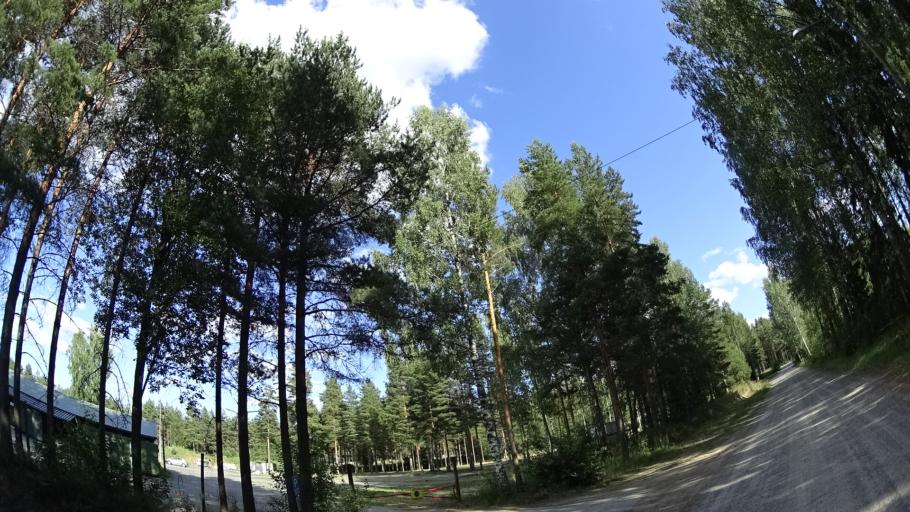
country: FI
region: Uusimaa
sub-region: Helsinki
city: Vihti
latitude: 60.3634
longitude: 24.3528
